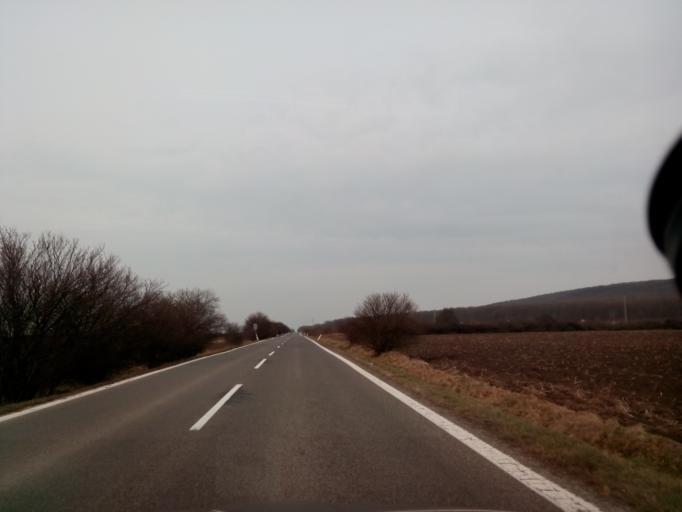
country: HU
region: Borsod-Abauj-Zemplen
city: Satoraljaujhely
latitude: 48.4915
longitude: 21.6487
